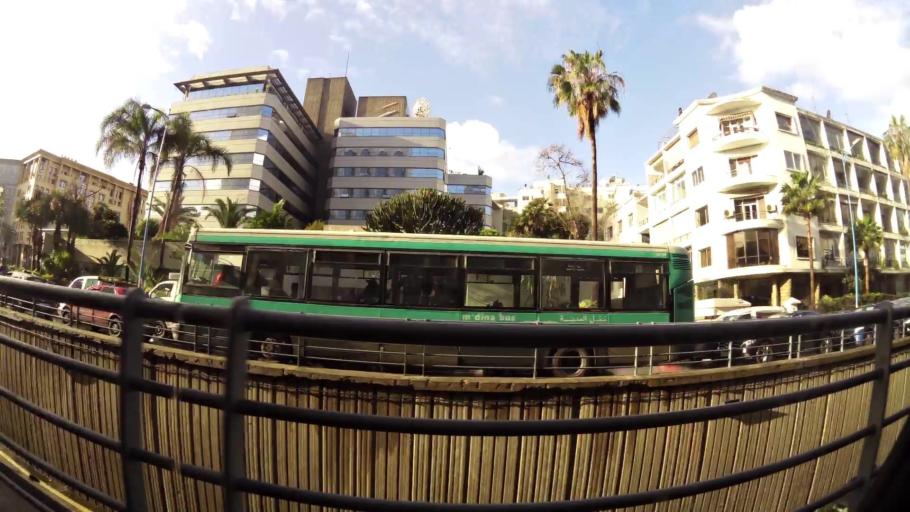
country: MA
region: Grand Casablanca
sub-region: Casablanca
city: Casablanca
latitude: 33.5836
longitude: -7.6244
